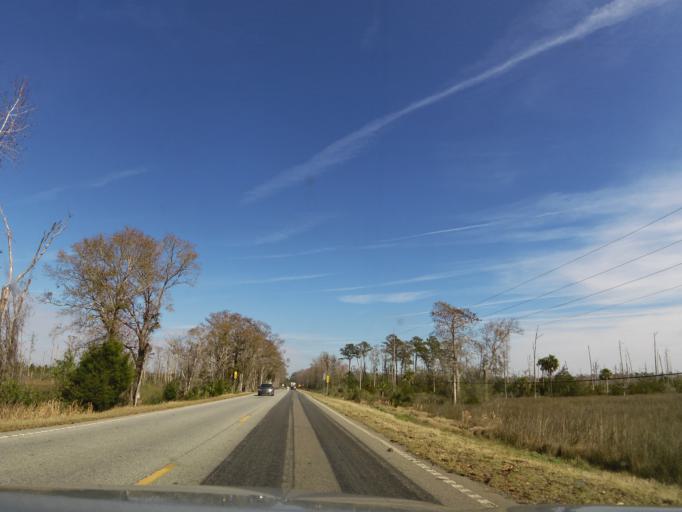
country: US
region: Georgia
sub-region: Glynn County
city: Dock Junction
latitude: 31.2661
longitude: -81.5910
